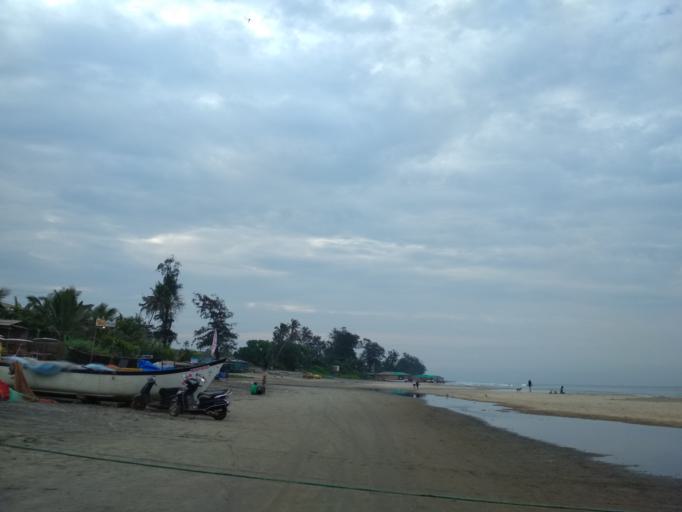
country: IN
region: Goa
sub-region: North Goa
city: Arambol
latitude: 15.6887
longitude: 73.7026
